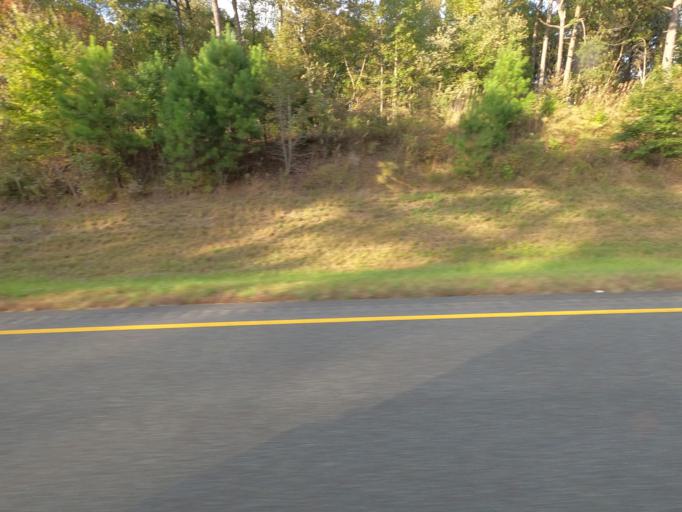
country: US
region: Tennessee
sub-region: Decatur County
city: Parsons
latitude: 35.8148
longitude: -88.2202
